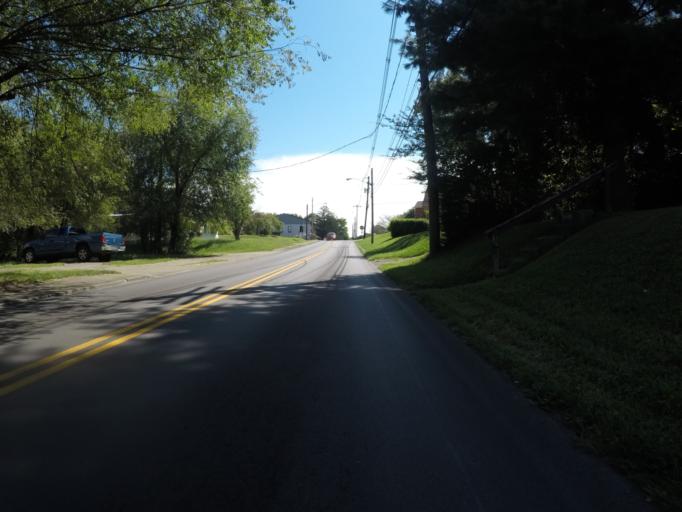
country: US
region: Kentucky
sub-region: Boyd County
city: Ashland
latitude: 38.4534
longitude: -82.6404
